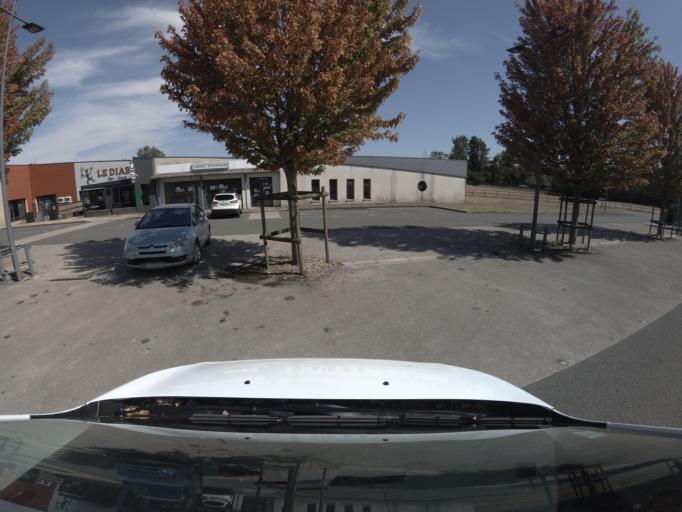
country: FR
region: Poitou-Charentes
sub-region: Departement des Deux-Sevres
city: Nueil-les-Aubiers
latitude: 46.9452
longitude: -0.5947
